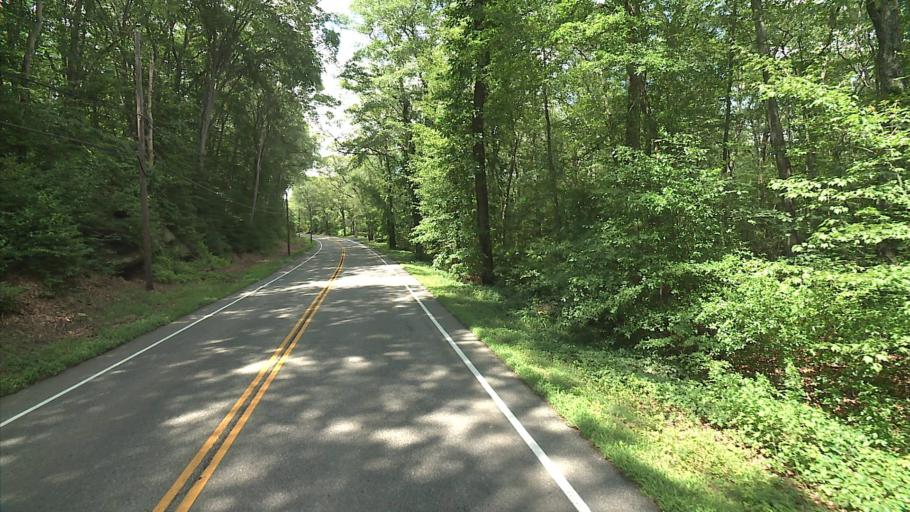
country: US
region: Connecticut
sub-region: Middlesex County
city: Clinton
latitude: 41.3282
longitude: -72.5498
